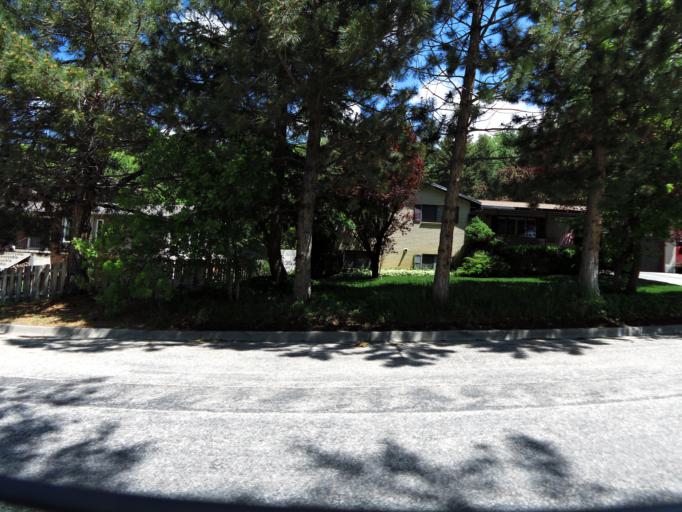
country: US
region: Utah
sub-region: Weber County
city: Uintah
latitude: 41.1582
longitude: -111.9177
